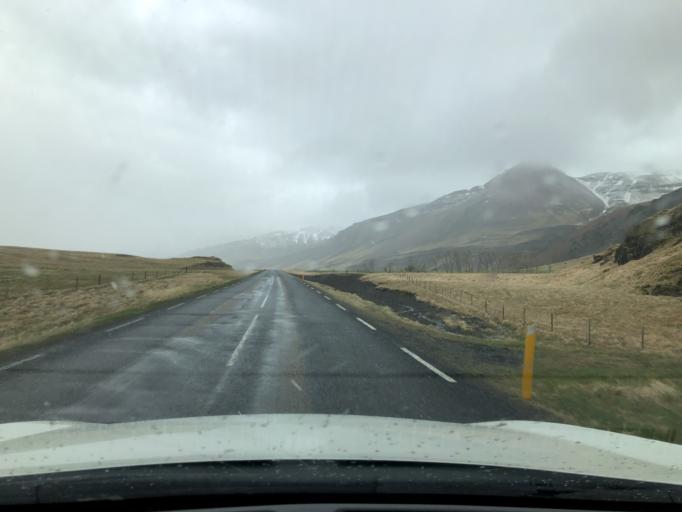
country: IS
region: East
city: Hoefn
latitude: 64.3449
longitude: -15.2469
